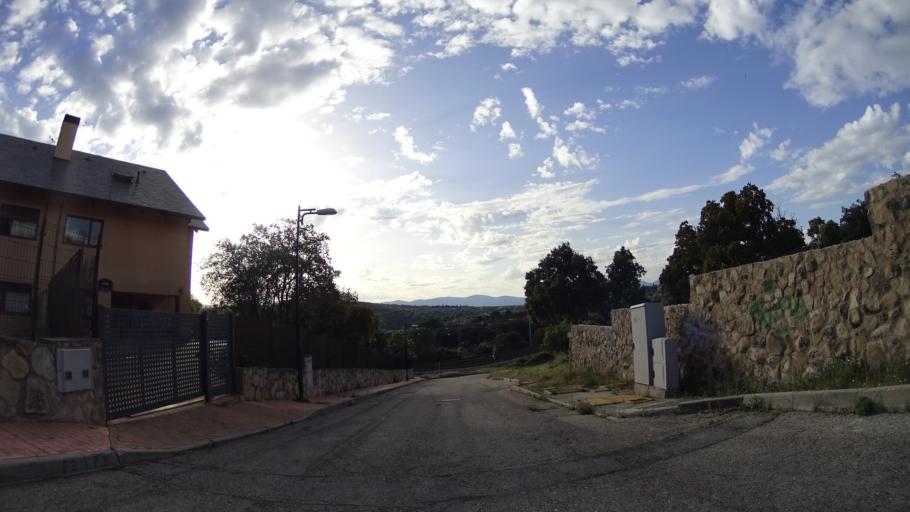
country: ES
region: Madrid
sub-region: Provincia de Madrid
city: Torrelodones
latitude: 40.5846
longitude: -3.9616
